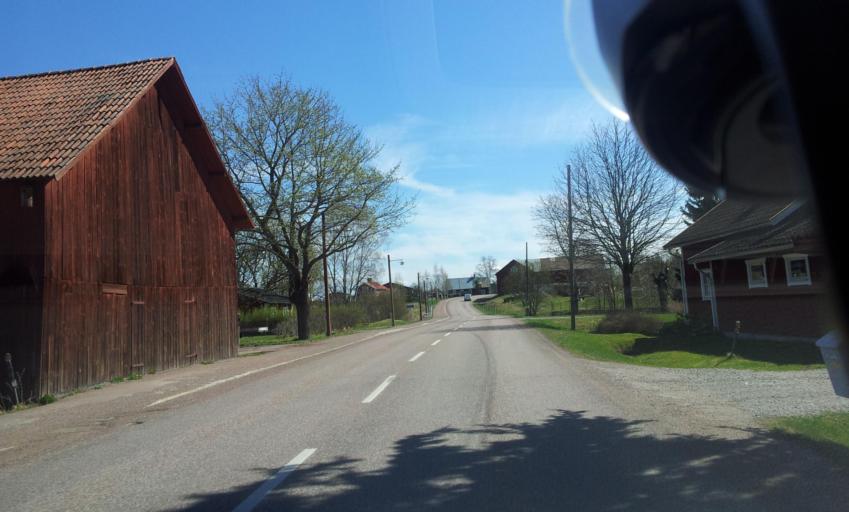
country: SE
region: Dalarna
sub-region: Borlange Kommun
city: Ornas
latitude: 60.4637
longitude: 15.5215
